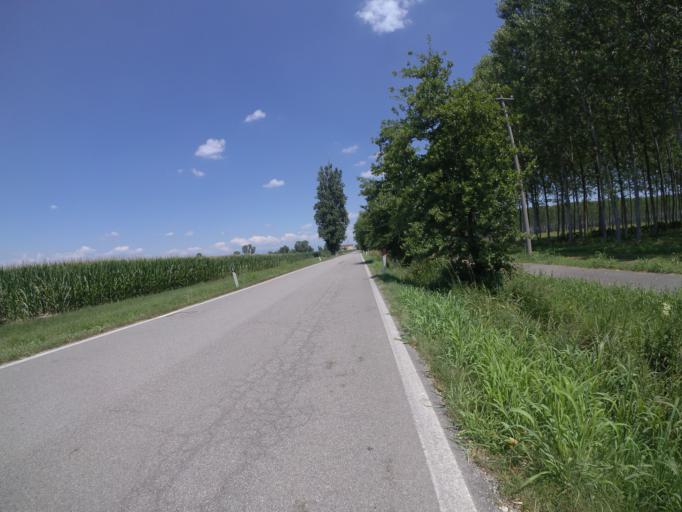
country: IT
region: Friuli Venezia Giulia
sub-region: Provincia di Udine
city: Varmo
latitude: 45.9259
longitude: 13.0010
